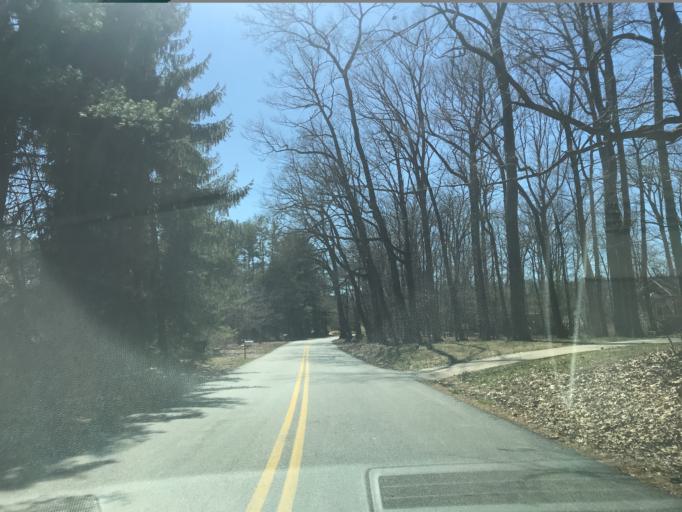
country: US
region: Pennsylvania
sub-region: York County
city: New Freedom
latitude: 39.6853
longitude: -76.6509
